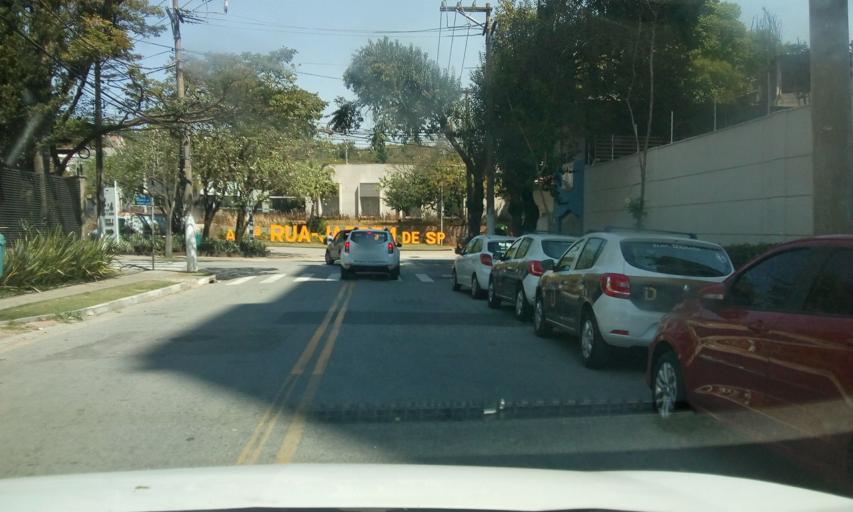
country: BR
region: Sao Paulo
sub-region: Osasco
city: Osasco
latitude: -23.5171
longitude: -46.7183
